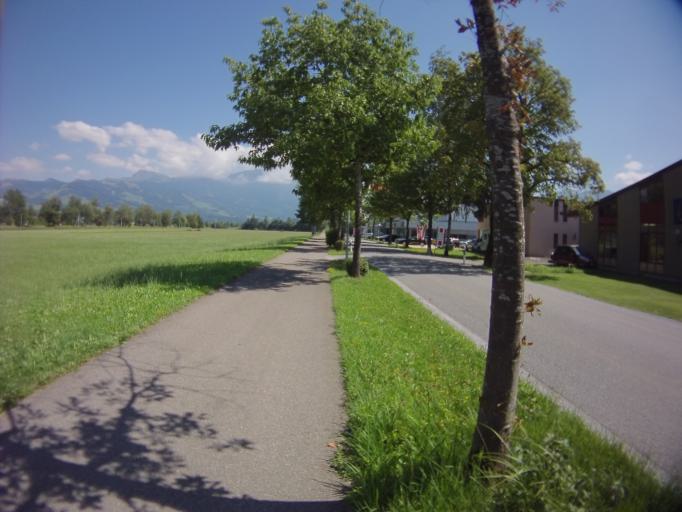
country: CH
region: Saint Gallen
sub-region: Wahlkreis See-Gaster
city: Uznach
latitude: 47.2206
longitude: 8.9858
